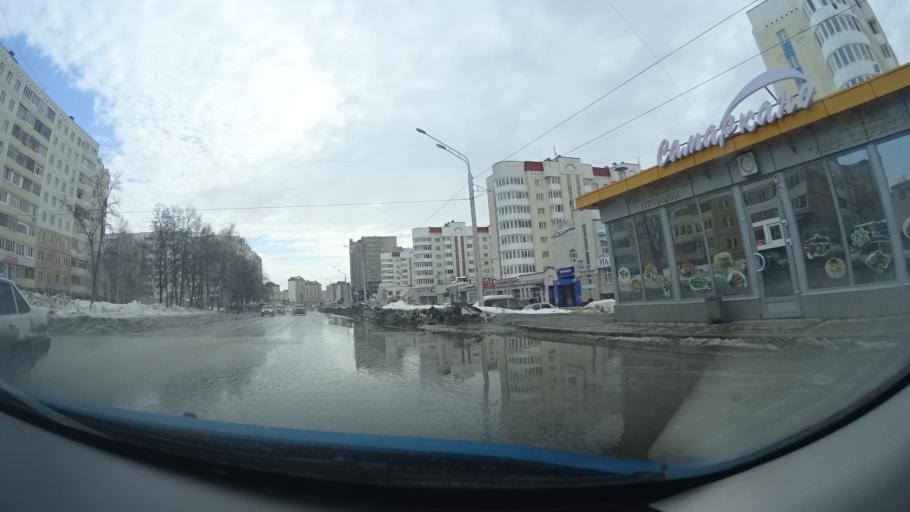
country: RU
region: Bashkortostan
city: Ufa
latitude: 54.6988
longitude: 55.9867
